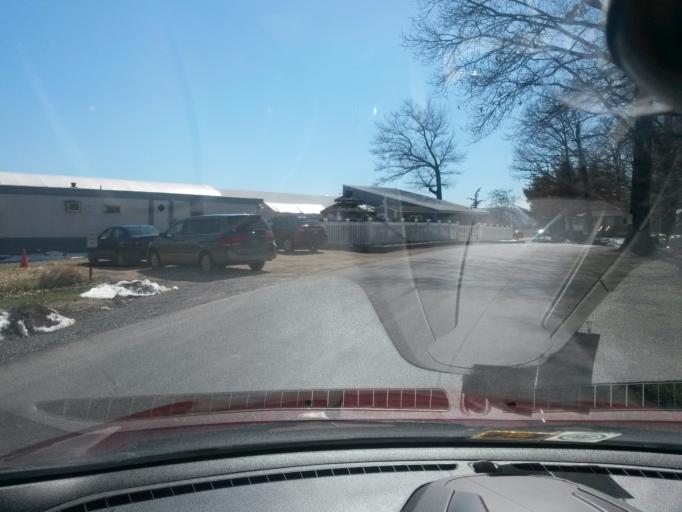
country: US
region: Virginia
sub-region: Augusta County
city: Stuarts Draft
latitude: 38.0422
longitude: -79.0065
